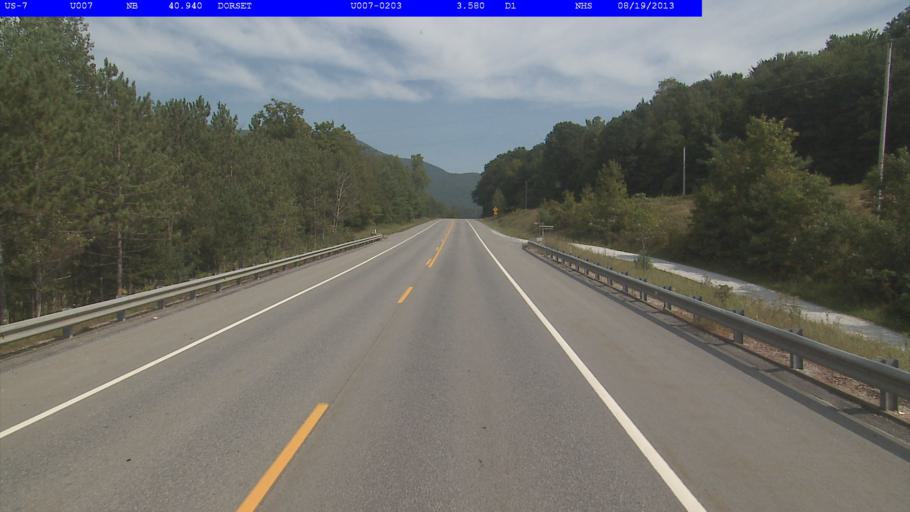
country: US
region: Vermont
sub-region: Bennington County
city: Manchester Center
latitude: 43.2608
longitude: -73.0079
